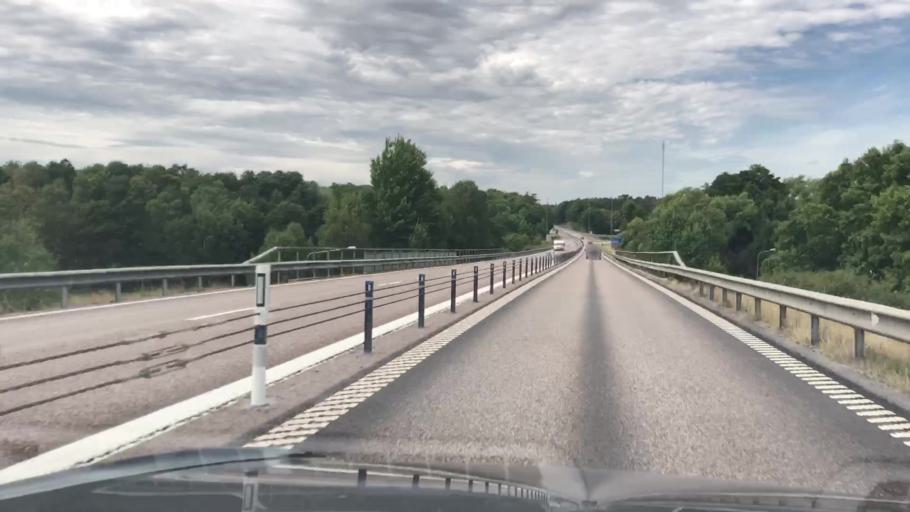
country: SE
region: Blekinge
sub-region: Ronneby Kommun
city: Brakne-Hoby
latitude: 56.2044
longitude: 15.0141
